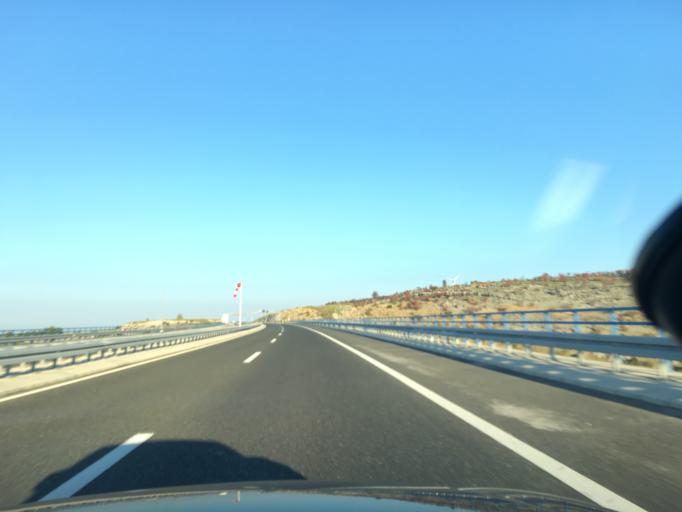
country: HR
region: Sibensko-Kniniska
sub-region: Grad Sibenik
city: Brodarica
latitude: 43.6942
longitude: 16.0320
